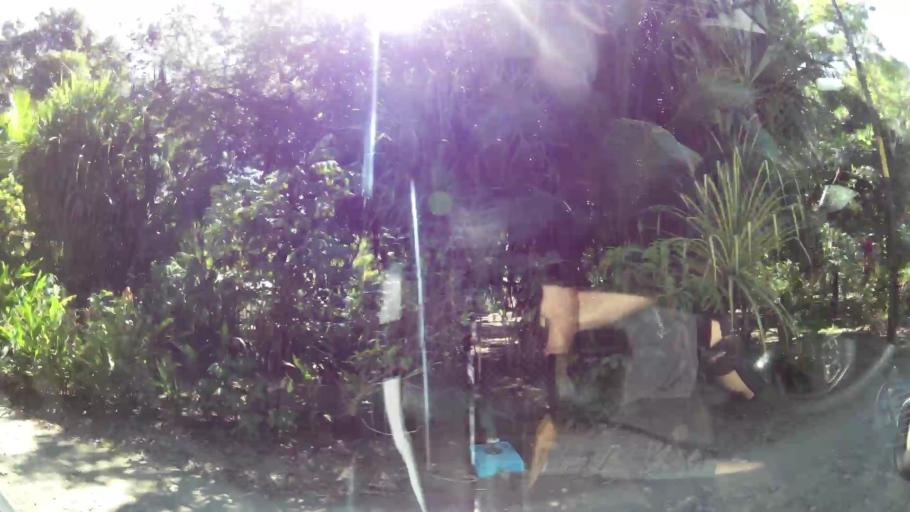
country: CR
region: Puntarenas
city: Quepos
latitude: 9.3210
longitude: -83.9622
